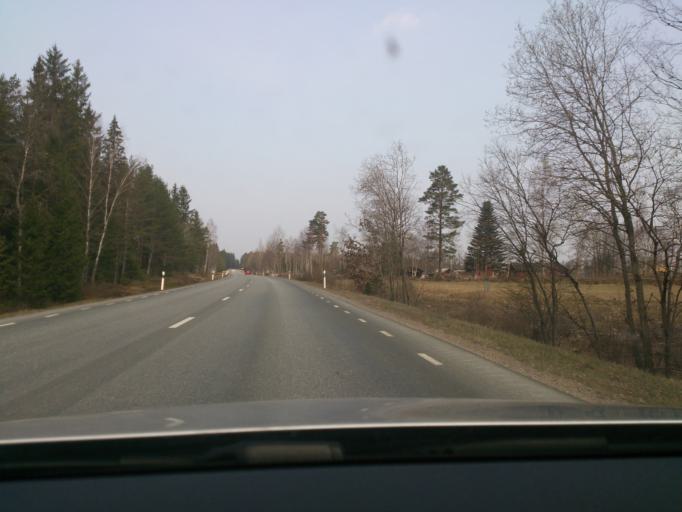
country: SE
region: Kronoberg
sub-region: Alvesta Kommun
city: Moheda
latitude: 56.9834
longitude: 14.5669
